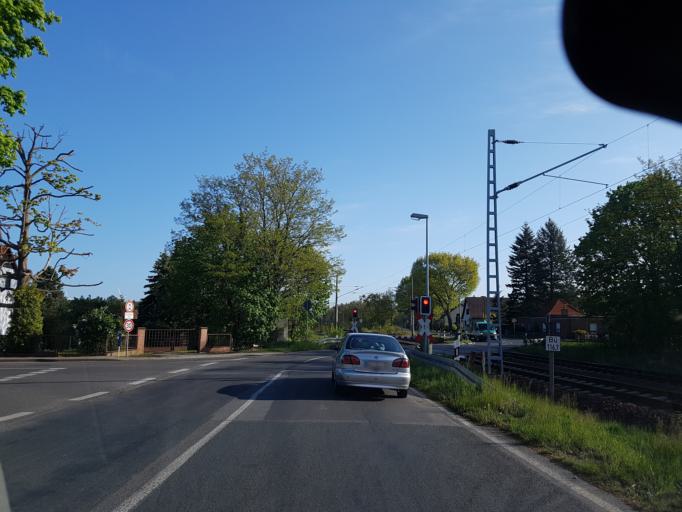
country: DE
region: Brandenburg
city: Grossraschen
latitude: 51.5975
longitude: 14.0147
